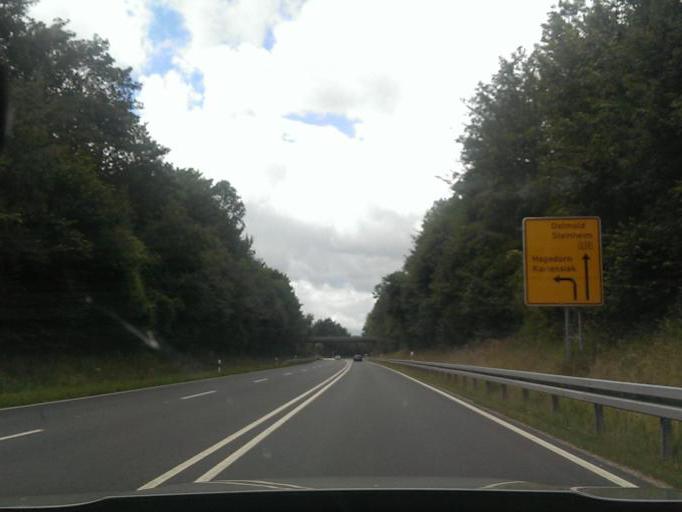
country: DE
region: North Rhine-Westphalia
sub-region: Regierungsbezirk Detmold
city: Schieder-Schwalenberg
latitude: 51.8444
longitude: 9.1714
